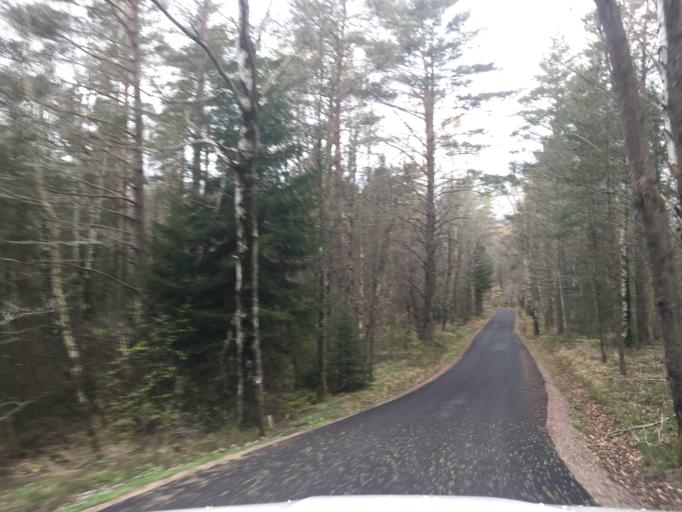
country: SE
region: Vaestra Goetaland
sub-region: Kungalvs Kommun
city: Kungalv
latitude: 57.8457
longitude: 11.9899
